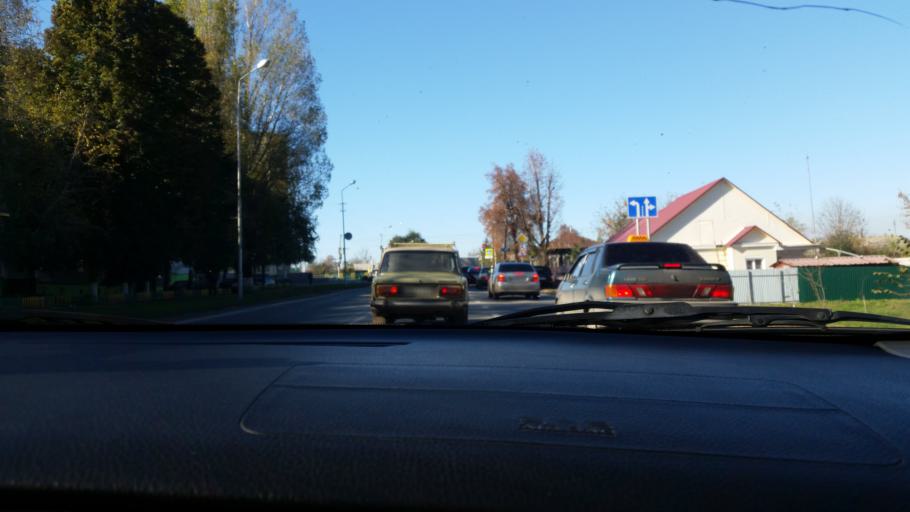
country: RU
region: Lipetsk
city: Gryazi
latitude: 52.4925
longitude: 39.9583
